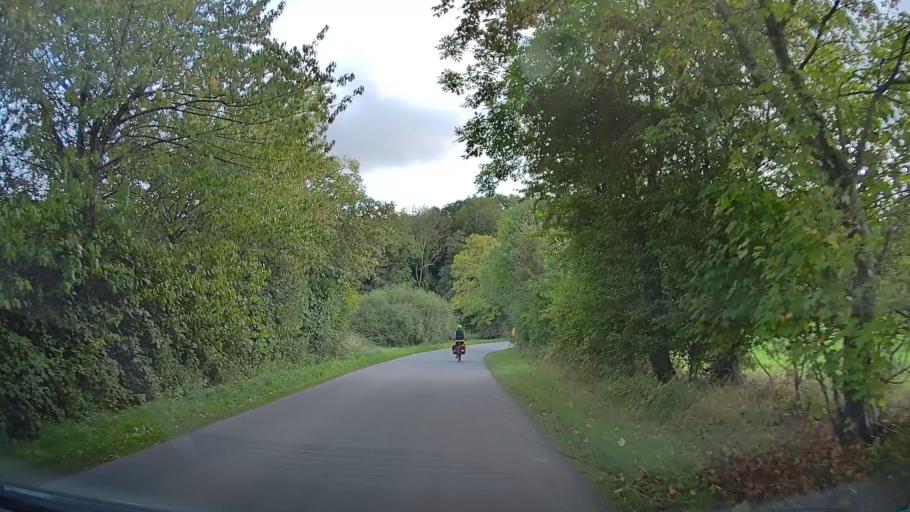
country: DE
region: Schleswig-Holstein
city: Steinberg
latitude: 54.7878
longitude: 9.7795
